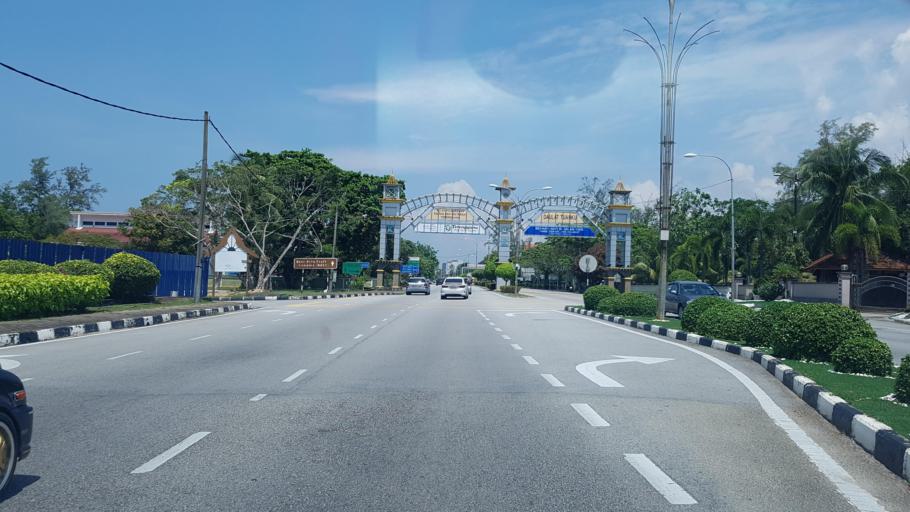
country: MY
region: Terengganu
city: Kuala Terengganu
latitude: 5.3184
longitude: 103.1537
